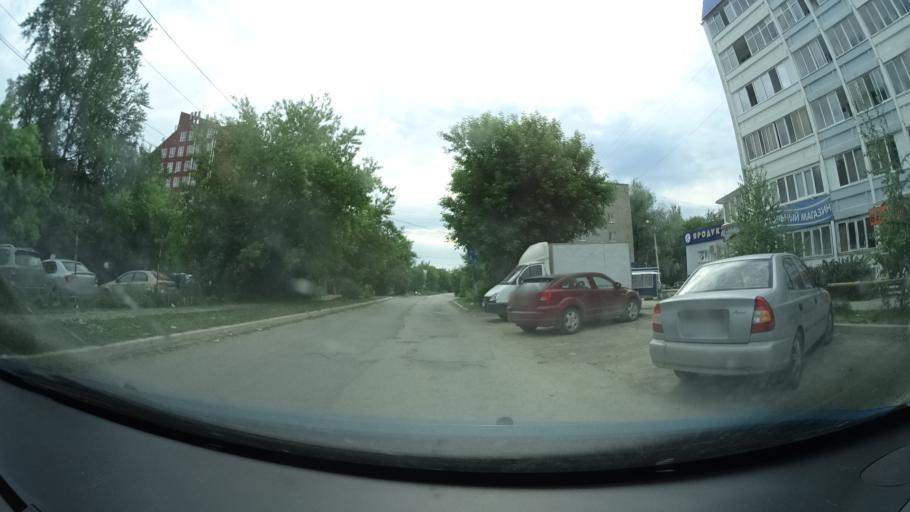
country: RU
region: Perm
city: Perm
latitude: 58.0213
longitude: 56.2721
